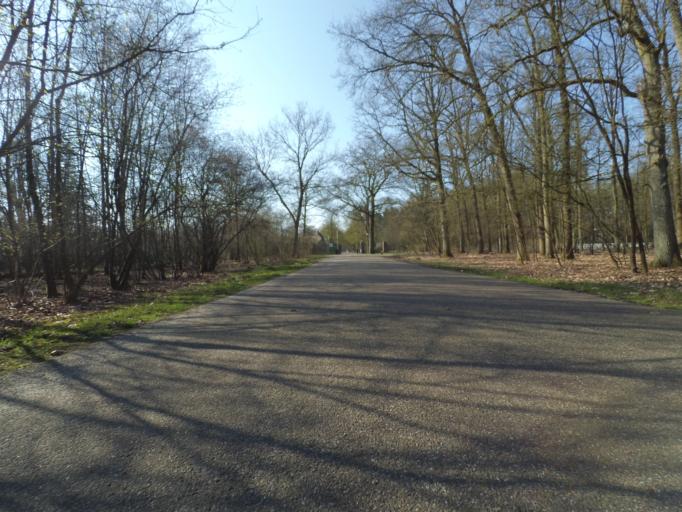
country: NL
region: Gelderland
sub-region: Gemeente Arnhem
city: Hoogkamp
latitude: 52.0344
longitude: 5.8672
